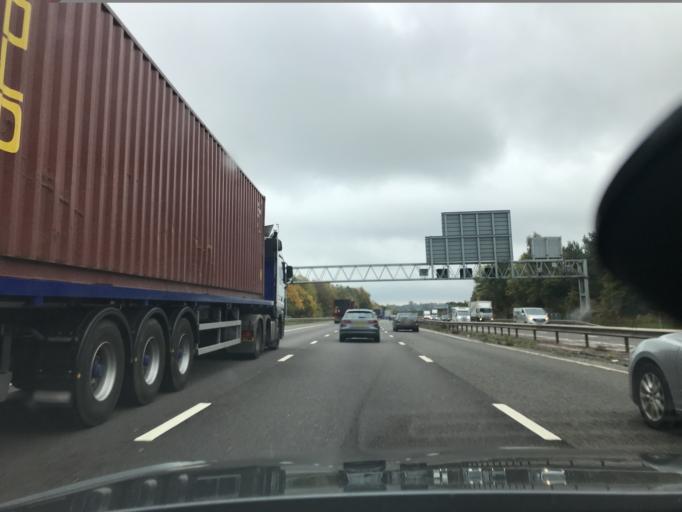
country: GB
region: England
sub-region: Solihull
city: Cheswick Green
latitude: 52.3439
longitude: -1.7927
